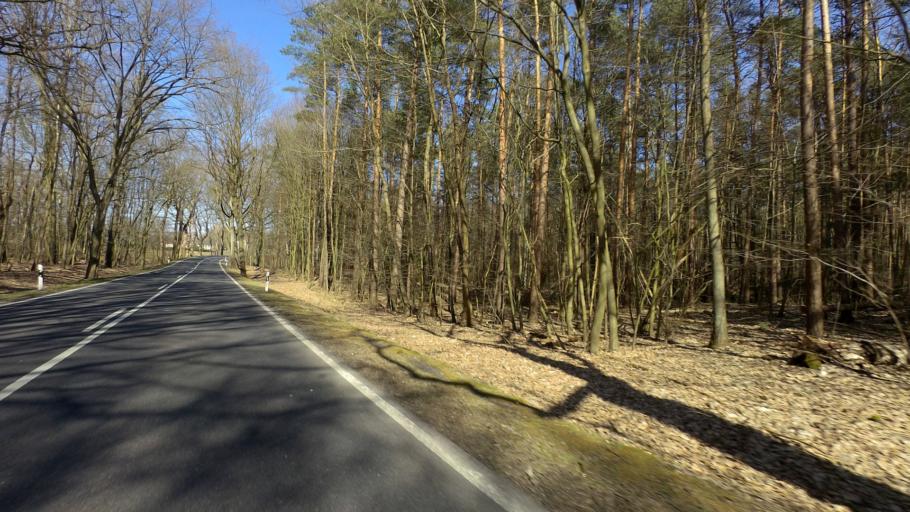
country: DE
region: Brandenburg
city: Werftpfuhl
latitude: 52.6776
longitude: 13.8344
